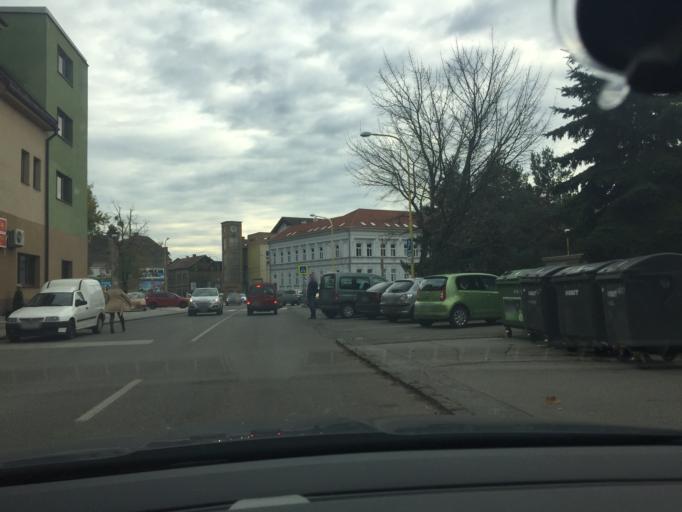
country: SK
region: Kosicky
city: Kosice
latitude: 48.7292
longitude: 21.2606
